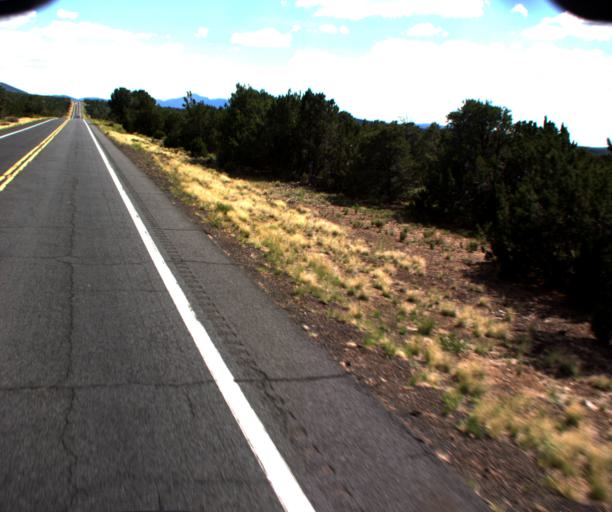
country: US
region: Arizona
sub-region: Coconino County
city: Williams
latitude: 35.4140
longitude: -112.1701
